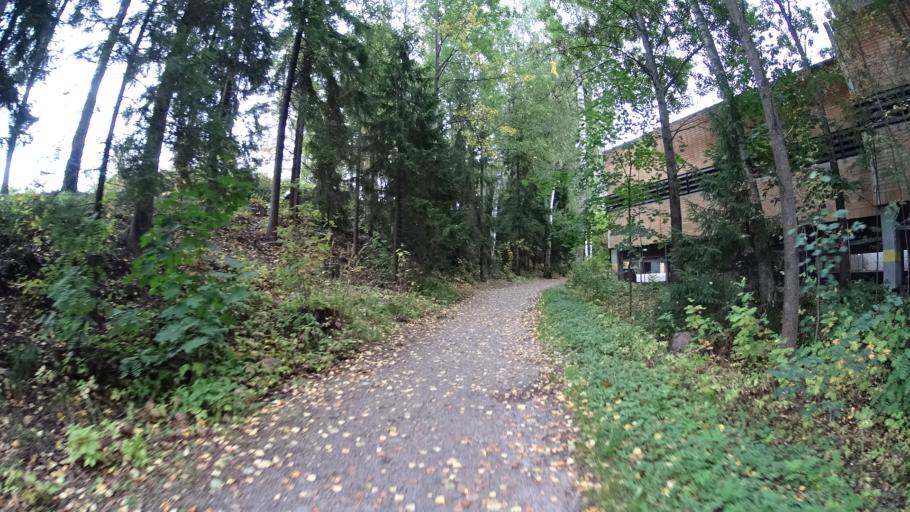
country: FI
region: Uusimaa
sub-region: Helsinki
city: Teekkarikylae
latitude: 60.2342
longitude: 24.8863
